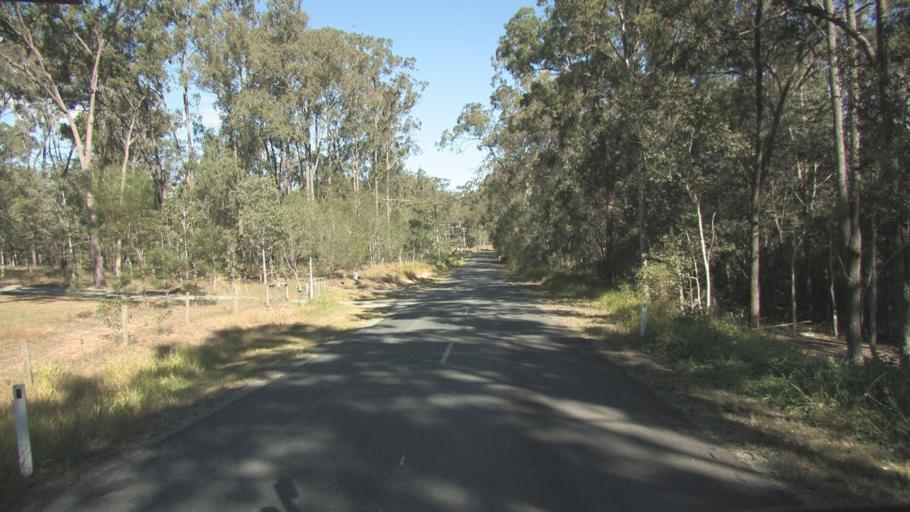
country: AU
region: Queensland
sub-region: Logan
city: Chambers Flat
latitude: -27.8137
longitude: 153.0713
